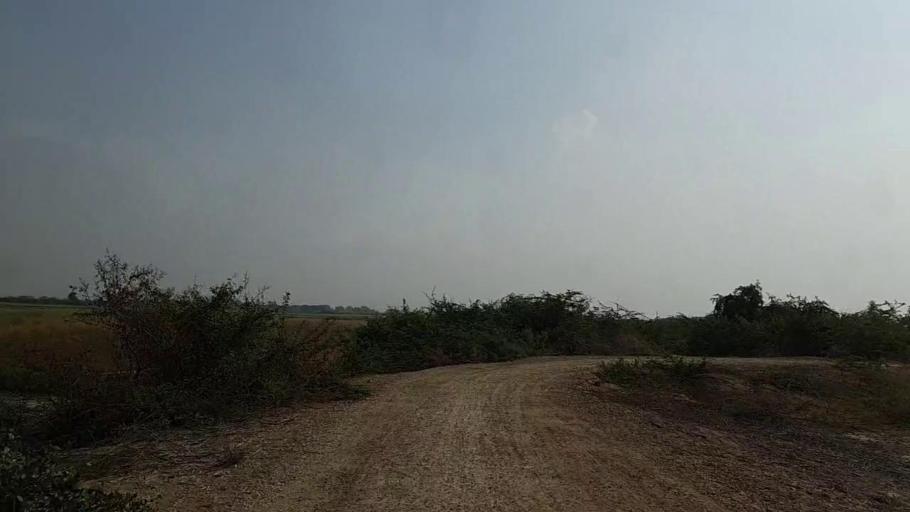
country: PK
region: Sindh
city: Naukot
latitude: 24.7580
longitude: 69.3065
